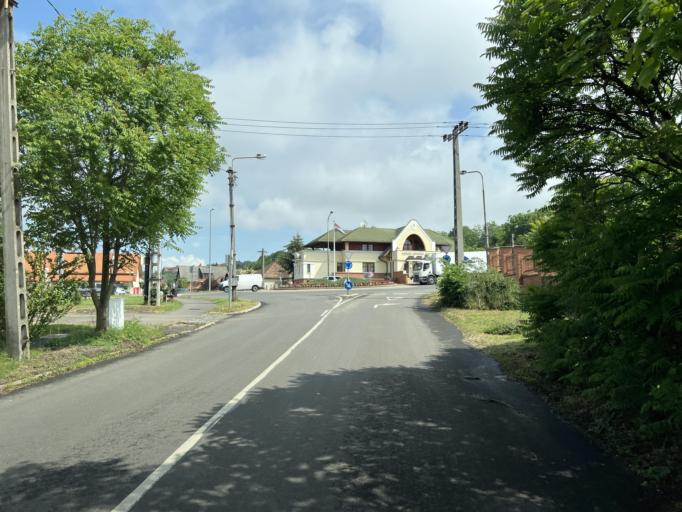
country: HU
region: Pest
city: Aszod
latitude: 47.6513
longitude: 19.4895
